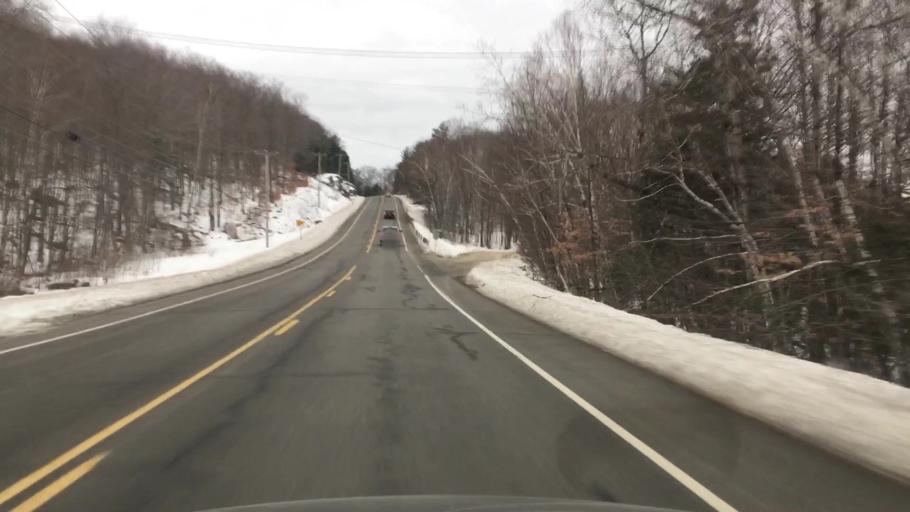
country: US
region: New Hampshire
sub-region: Merrimack County
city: Newbury
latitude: 43.3333
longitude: -72.0477
